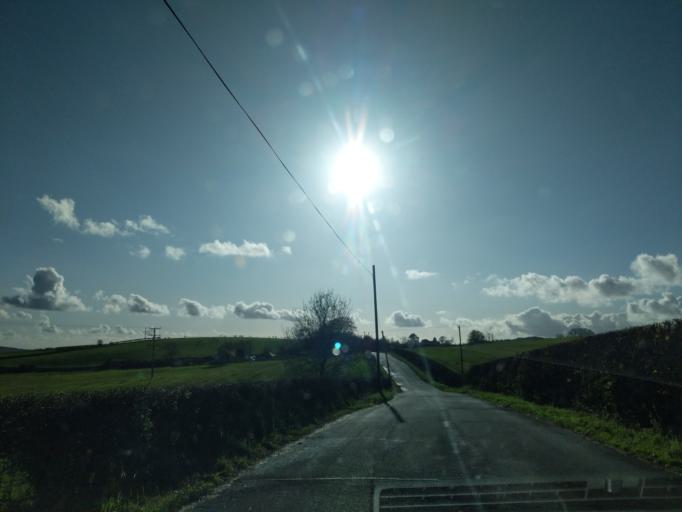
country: GB
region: Scotland
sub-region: Dumfries and Galloway
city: Dalbeattie
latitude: 55.0201
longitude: -3.7942
